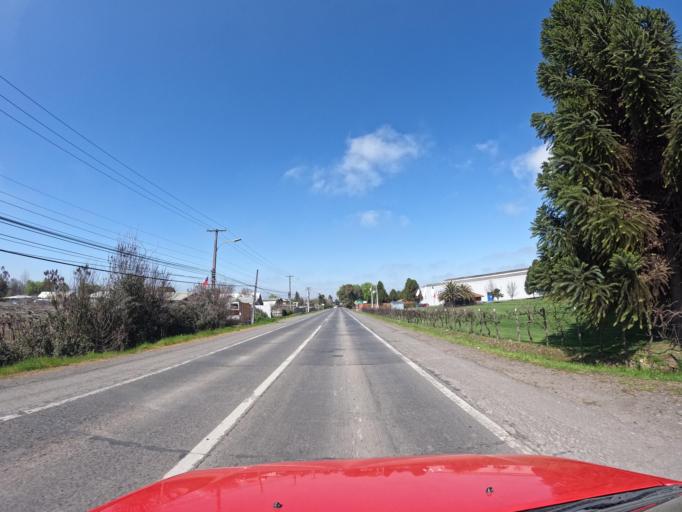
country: CL
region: Maule
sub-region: Provincia de Curico
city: Molina
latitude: -35.0656
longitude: -71.2563
